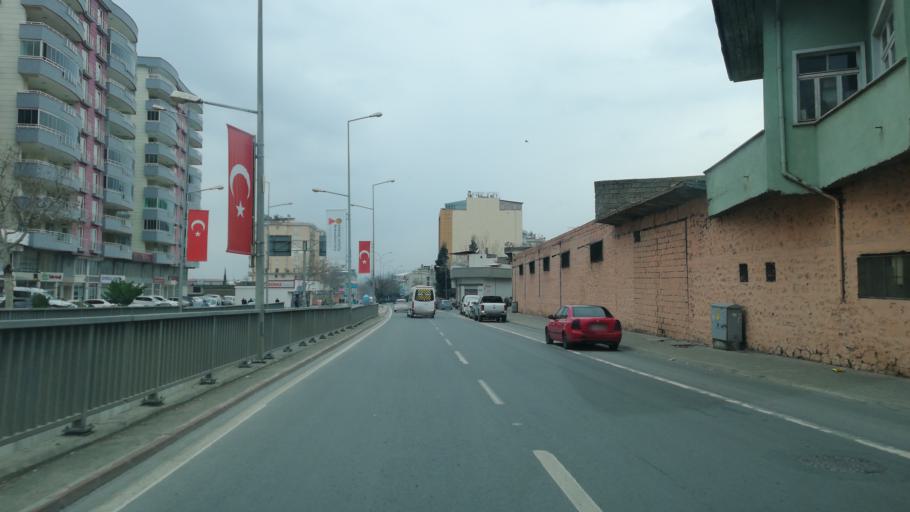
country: TR
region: Kahramanmaras
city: Kahramanmaras
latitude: 37.5714
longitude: 36.9414
